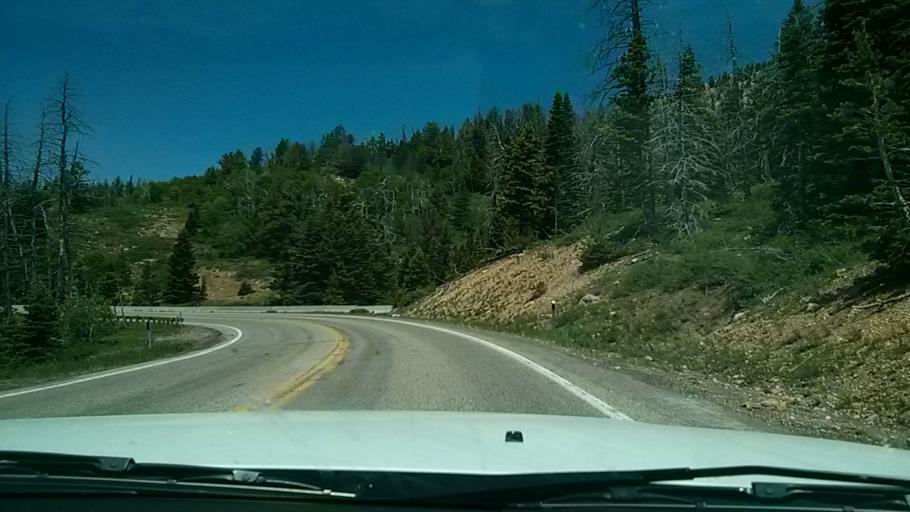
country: US
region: Utah
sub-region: Iron County
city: Cedar City
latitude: 37.5805
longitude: -112.8727
